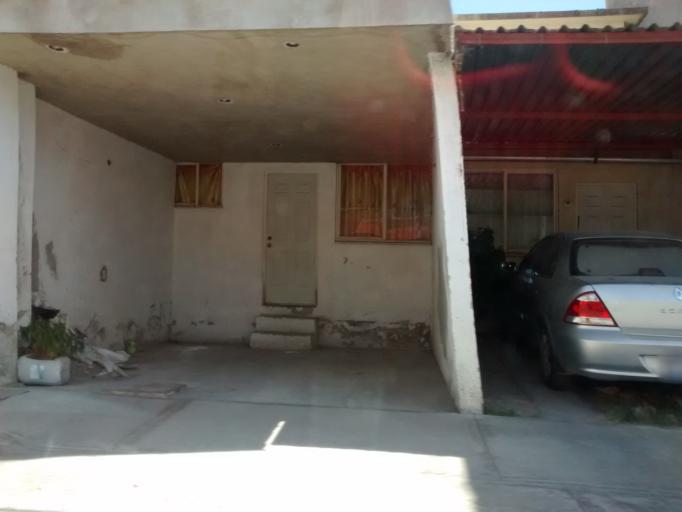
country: MX
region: Puebla
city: Tehuacan
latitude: 18.4709
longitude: -97.4130
